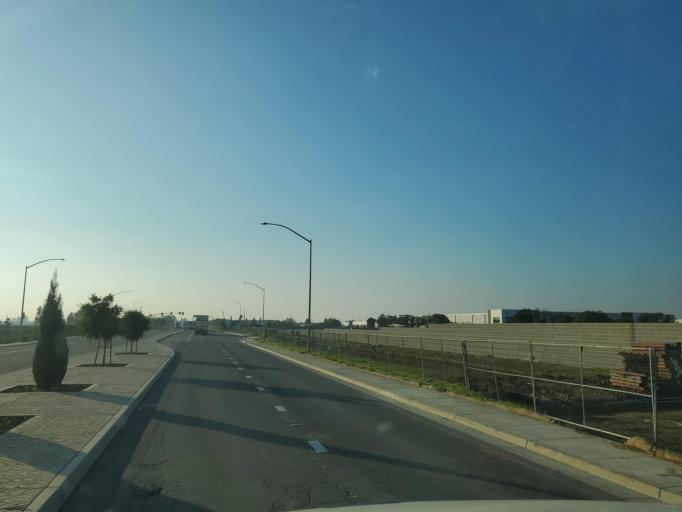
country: US
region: California
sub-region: San Joaquin County
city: Kennedy
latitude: 37.9053
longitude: -121.1994
